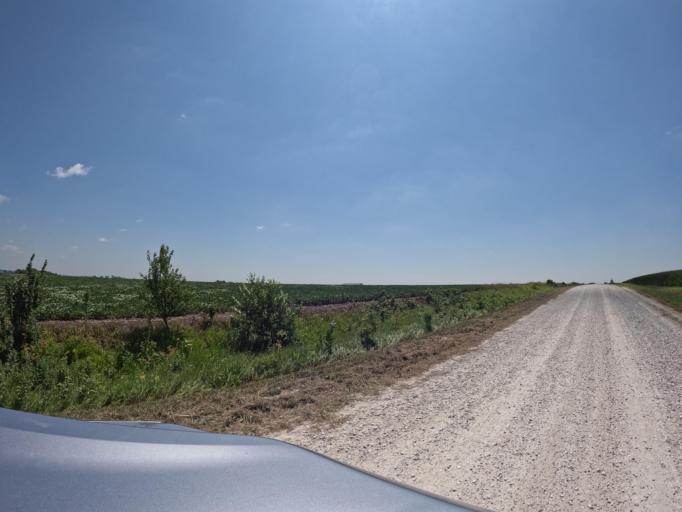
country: US
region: Iowa
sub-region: Keokuk County
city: Sigourney
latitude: 41.2816
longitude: -92.2381
